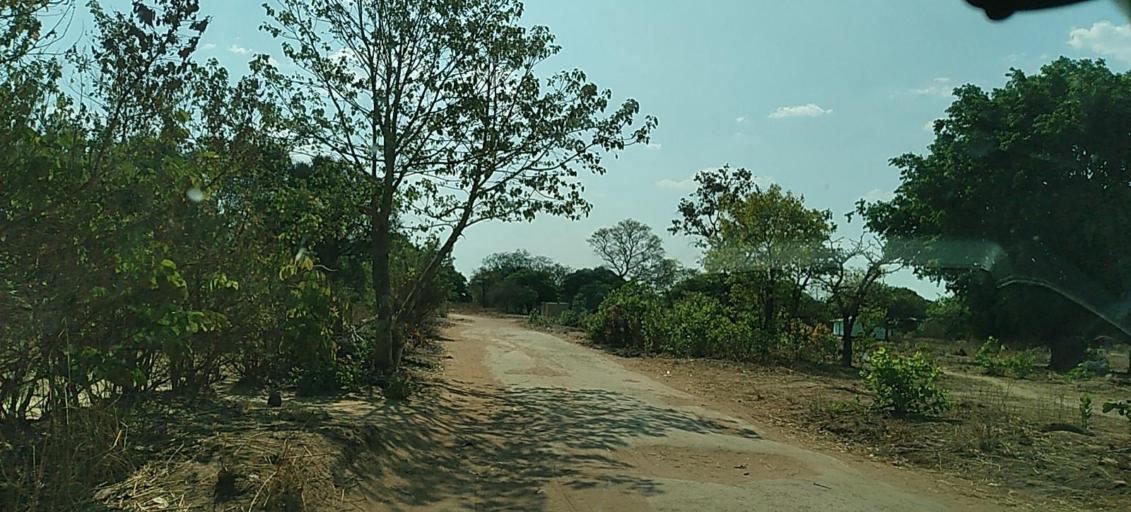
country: ZM
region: North-Western
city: Kalengwa
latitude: -13.1319
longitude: 25.0147
